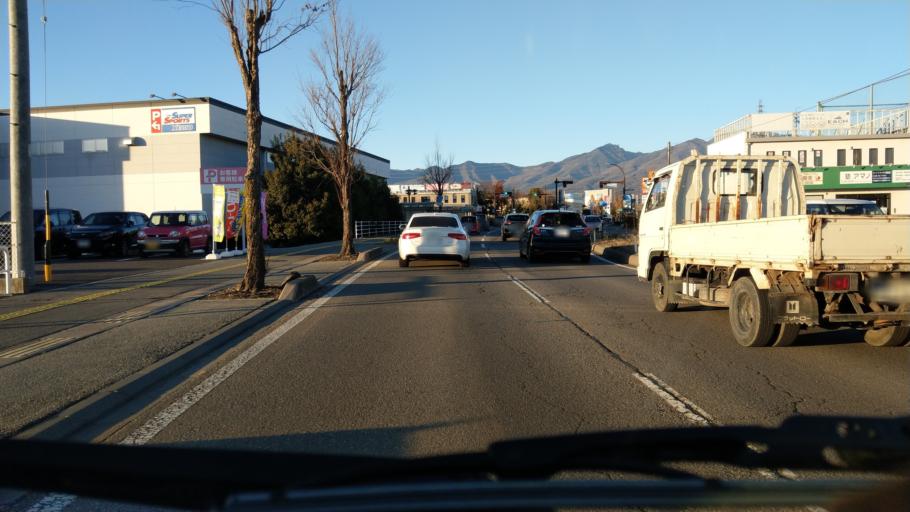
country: JP
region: Nagano
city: Komoro
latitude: 36.2729
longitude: 138.4655
